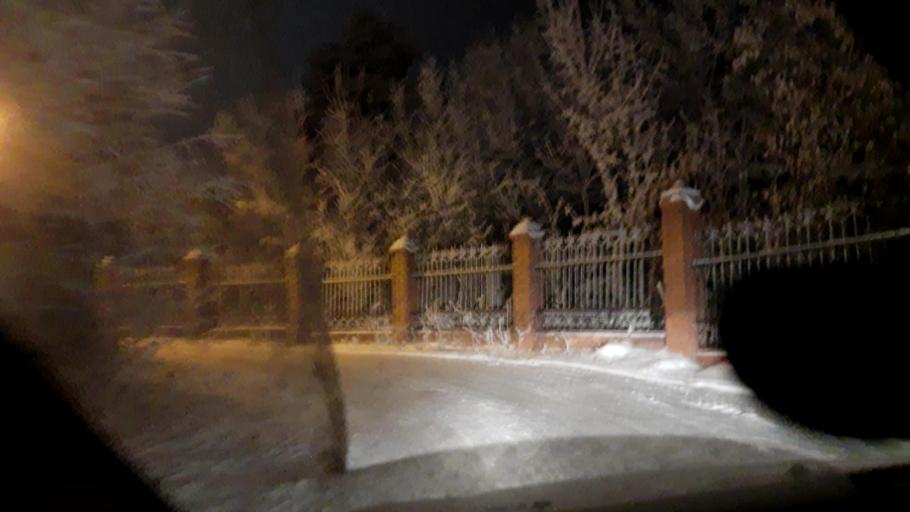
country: RU
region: Bashkortostan
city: Ufa
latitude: 54.7253
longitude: 55.9201
